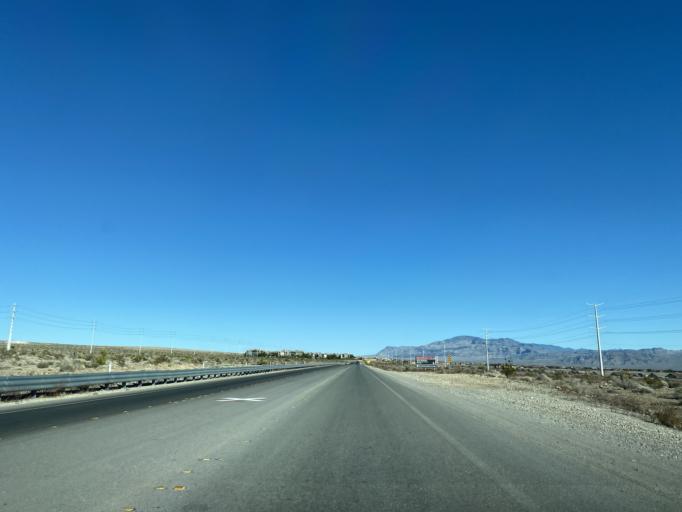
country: US
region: Nevada
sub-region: Clark County
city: Summerlin South
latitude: 36.2655
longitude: -115.3300
